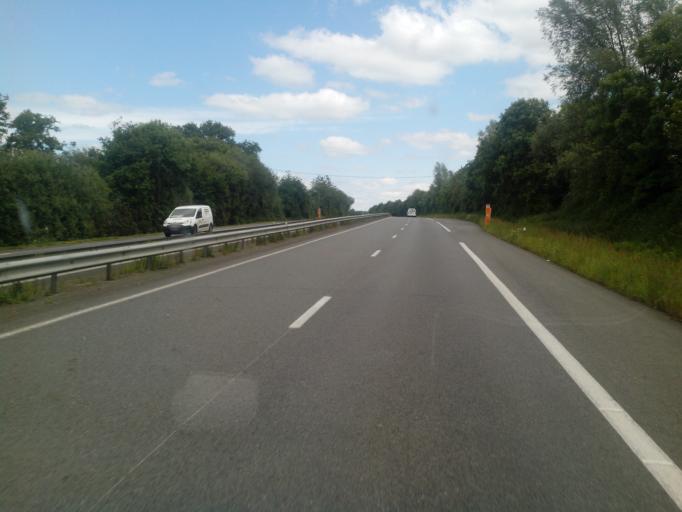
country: FR
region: Brittany
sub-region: Departement des Cotes-d'Armor
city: Pedernec
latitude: 48.5687
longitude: -3.2454
